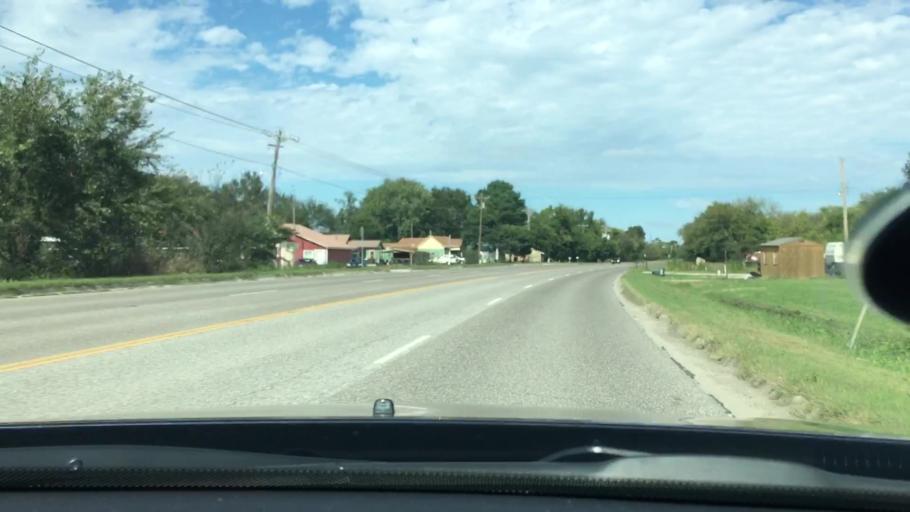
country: US
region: Oklahoma
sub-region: Murray County
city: Davis
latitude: 34.4860
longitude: -97.1303
